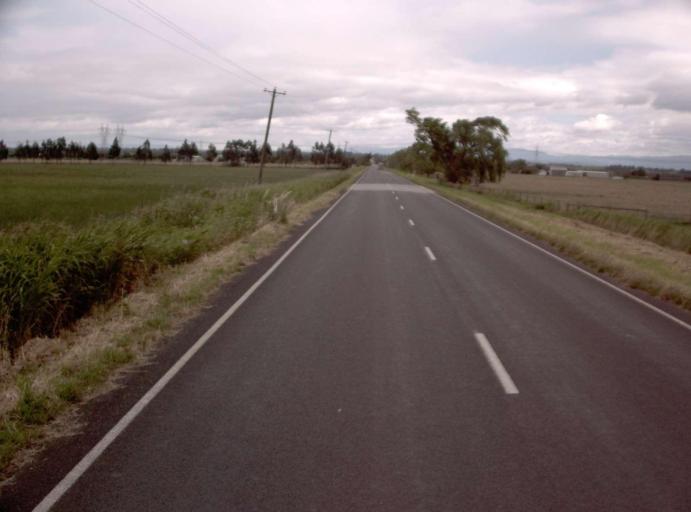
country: AU
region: Victoria
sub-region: Latrobe
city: Moe
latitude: -38.1952
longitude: 146.1504
